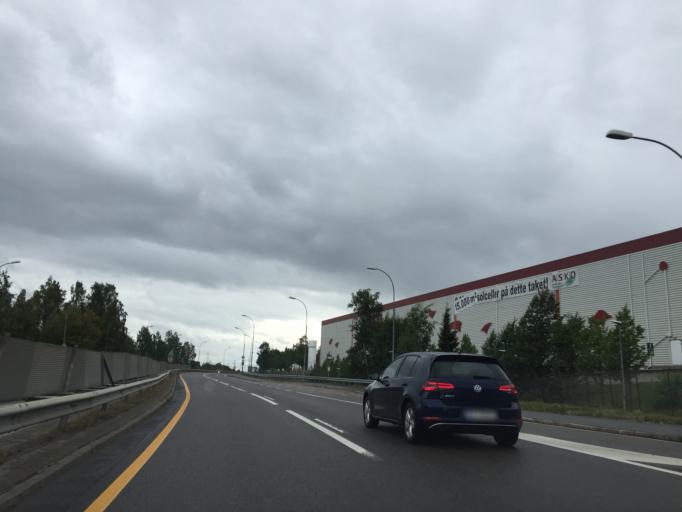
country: NO
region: Akershus
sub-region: Lorenskog
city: Kjenn
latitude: 59.9446
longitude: 10.8709
